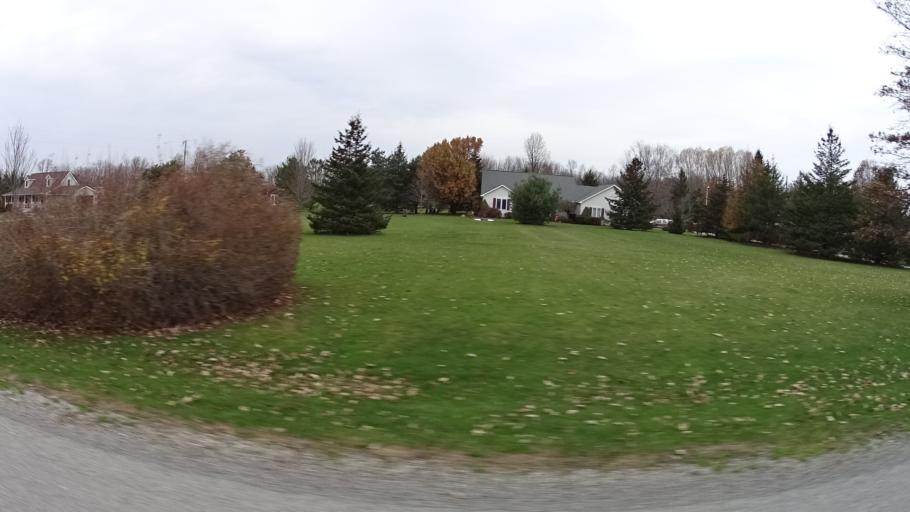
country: US
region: Ohio
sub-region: Lorain County
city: Lagrange
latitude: 41.1878
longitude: -82.0765
